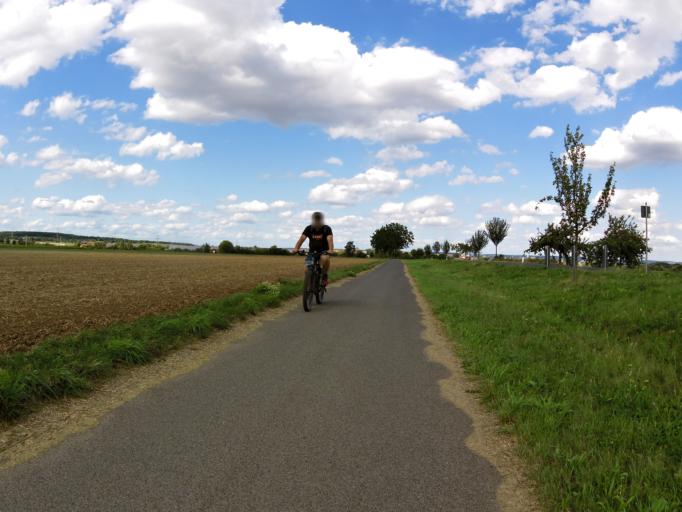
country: DE
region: Bavaria
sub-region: Regierungsbezirk Unterfranken
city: Bergrheinfeld
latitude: 49.9953
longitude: 10.1722
